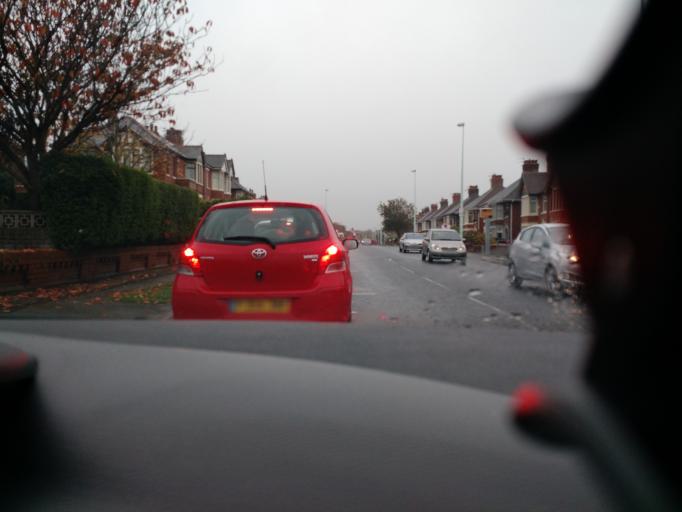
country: GB
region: England
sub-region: Lancashire
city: Great Marton
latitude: 53.8392
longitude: -3.0310
